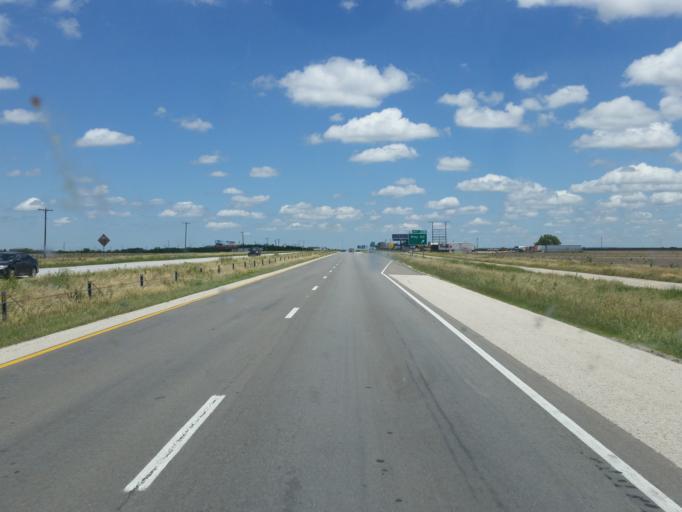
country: US
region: Texas
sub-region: Nolan County
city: Roscoe
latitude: 32.4486
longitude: -100.4925
